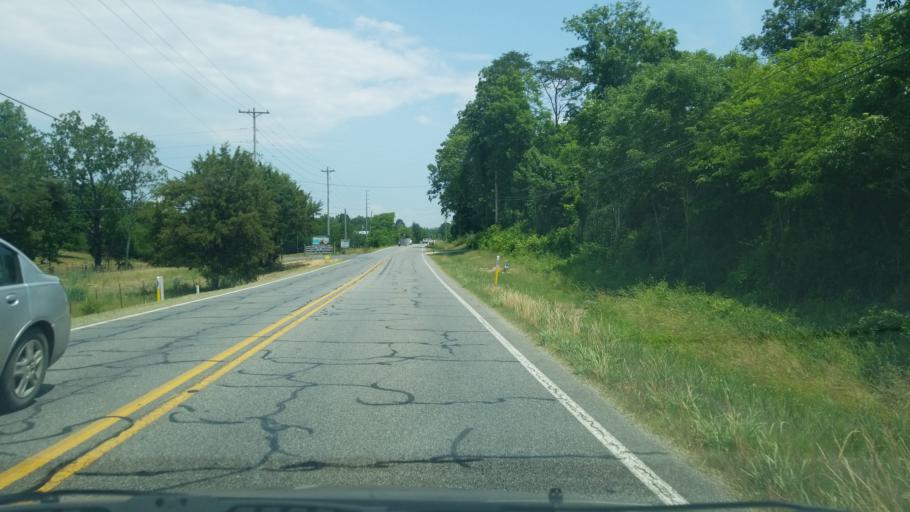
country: US
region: Tennessee
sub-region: Hamilton County
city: East Brainerd
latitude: 34.9708
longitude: -85.1007
